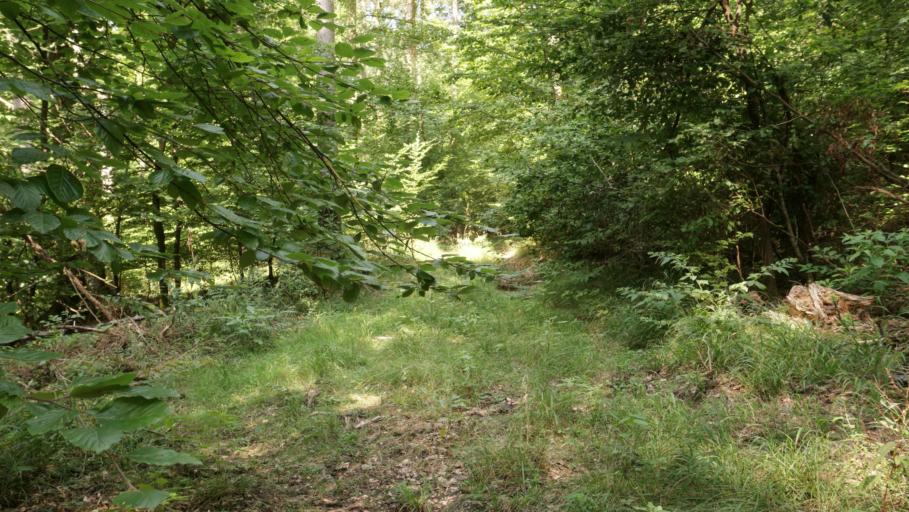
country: DE
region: Baden-Wuerttemberg
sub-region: Karlsruhe Region
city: Mosbach
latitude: 49.3879
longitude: 9.1553
